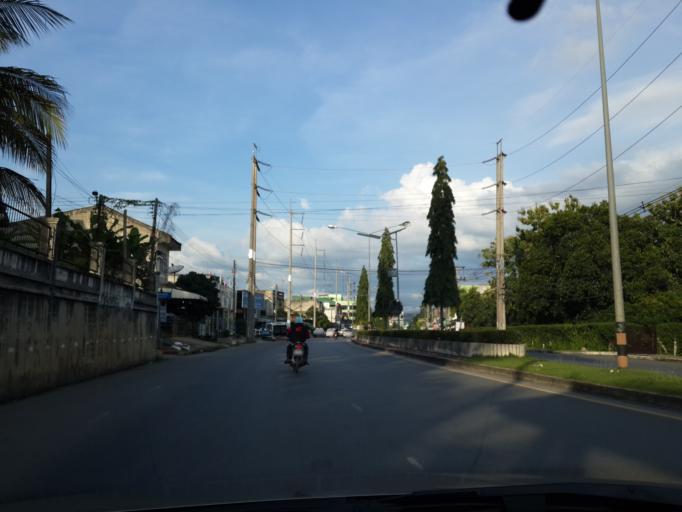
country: TH
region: Yala
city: Yala
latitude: 6.5463
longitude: 101.2737
